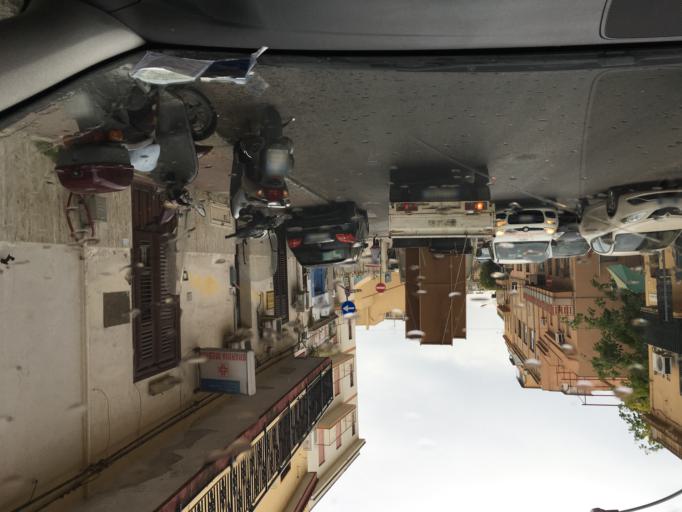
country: IT
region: Sicily
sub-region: Palermo
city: Isola delle Femmine
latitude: 38.1969
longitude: 13.3137
